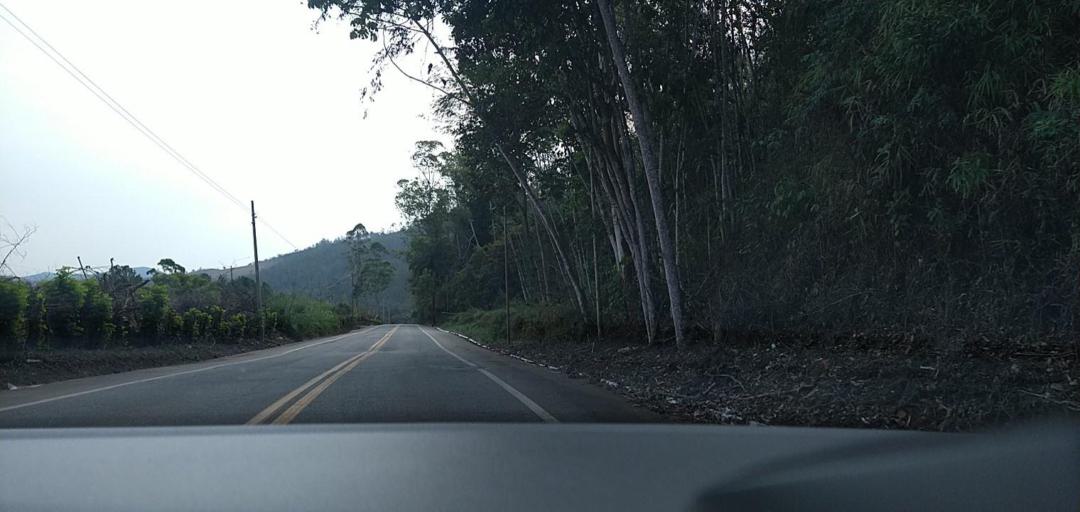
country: BR
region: Minas Gerais
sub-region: Rio Piracicaba
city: Rio Piracicaba
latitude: -19.8868
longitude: -43.1309
